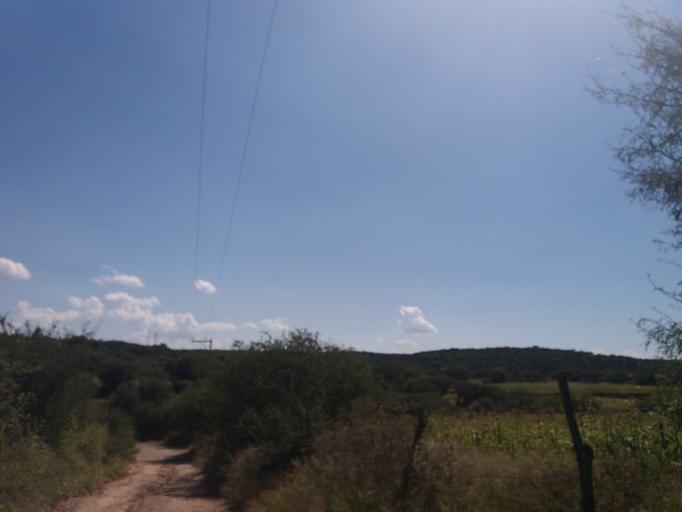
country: MX
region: Aguascalientes
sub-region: Aguascalientes
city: Penuelas (El Cienegal)
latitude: 21.7673
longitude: -102.2387
